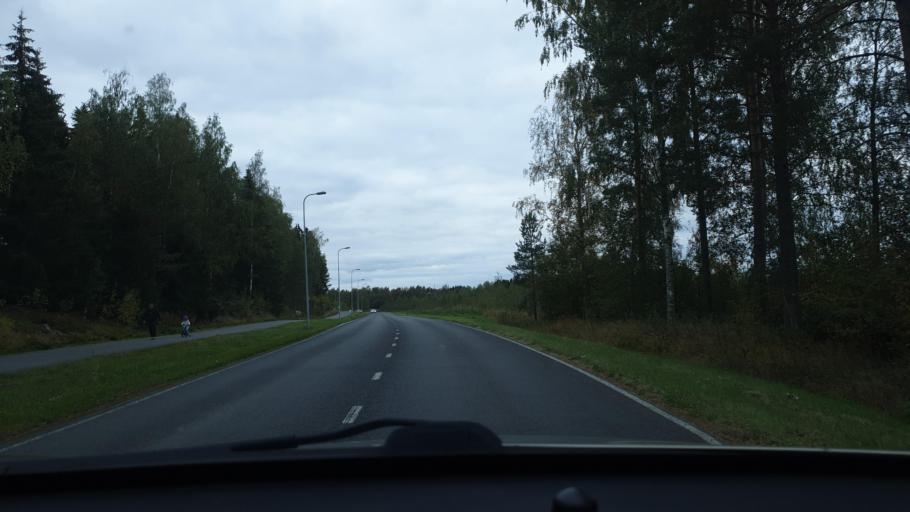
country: FI
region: Ostrobothnia
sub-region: Vaasa
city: Teeriniemi
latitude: 63.0976
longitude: 21.6983
